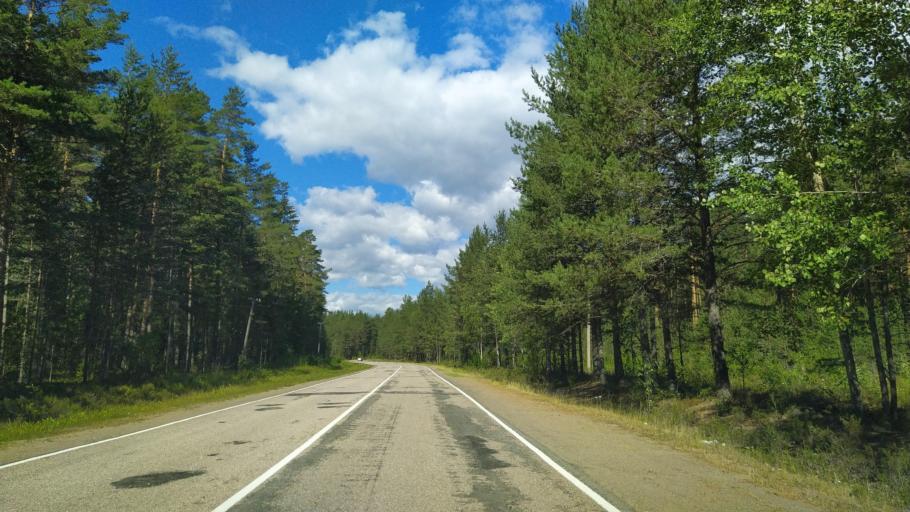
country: RU
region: Leningrad
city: Priozersk
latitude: 60.9779
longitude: 30.2756
